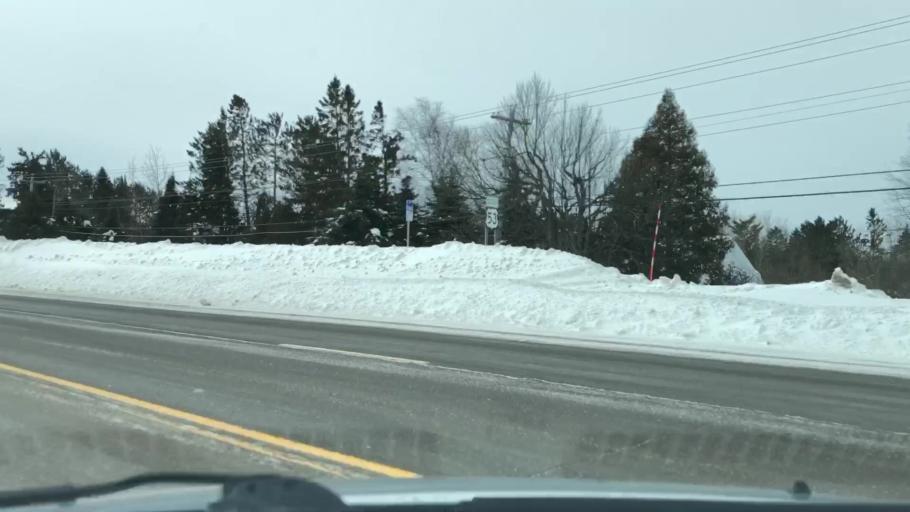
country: US
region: Minnesota
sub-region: Saint Louis County
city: Duluth
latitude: 46.7931
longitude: -92.1562
